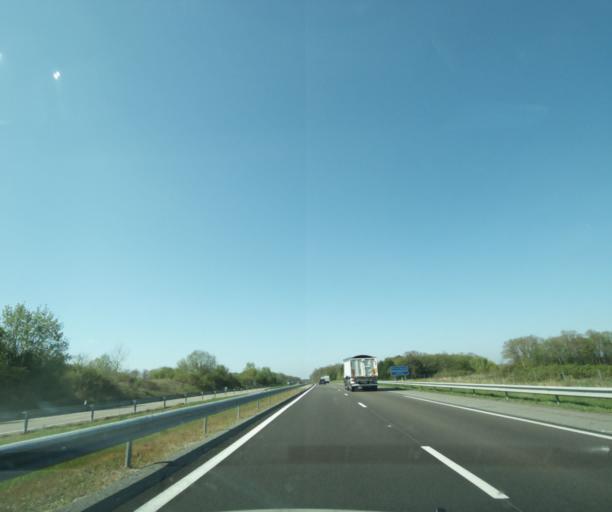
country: FR
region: Bourgogne
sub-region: Departement de la Nievre
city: Neuvy-sur-Loire
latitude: 47.4914
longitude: 2.9363
